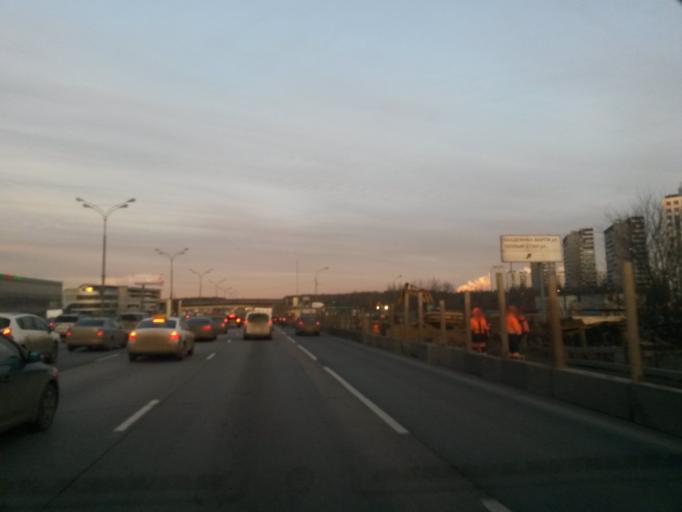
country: RU
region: Moskovskaya
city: Mosrentgen
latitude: 55.6281
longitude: 37.4726
